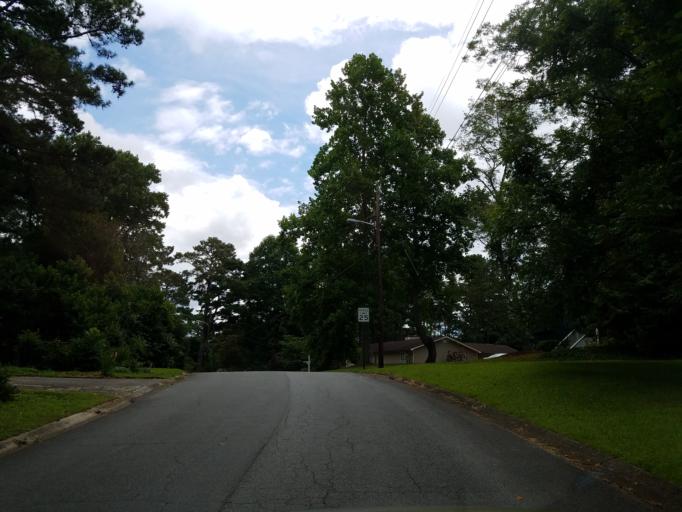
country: US
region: Georgia
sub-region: Cobb County
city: Marietta
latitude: 33.9513
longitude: -84.4866
